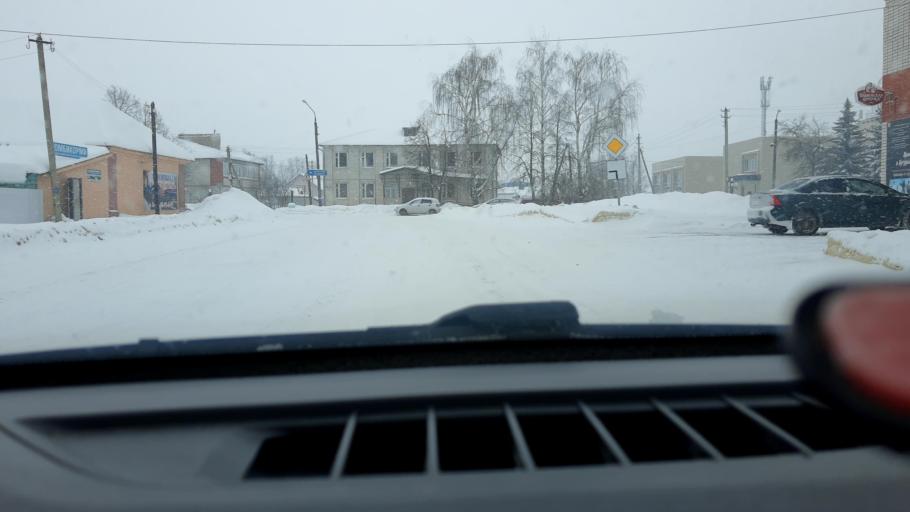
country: RU
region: Nizjnij Novgorod
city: Buturlino
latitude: 55.5679
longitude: 44.9064
